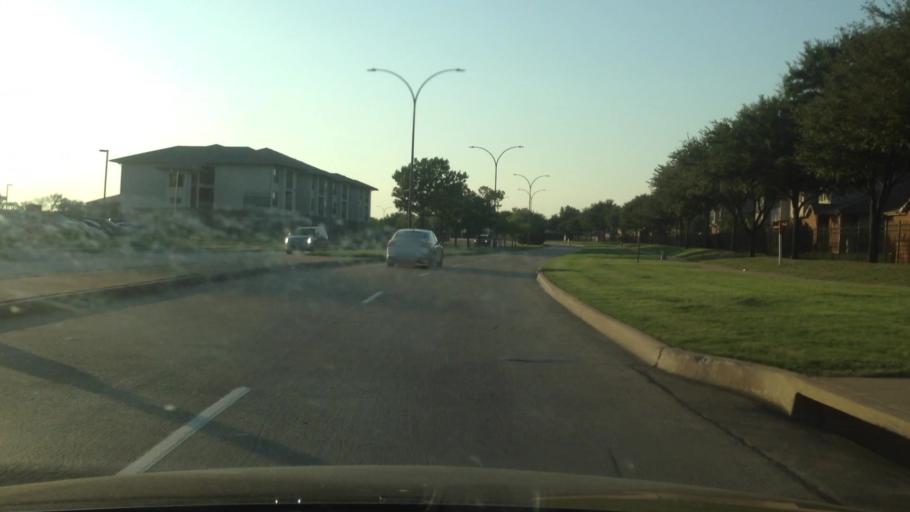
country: US
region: Texas
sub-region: Tarrant County
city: Dalworthington Gardens
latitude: 32.6458
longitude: -97.1244
